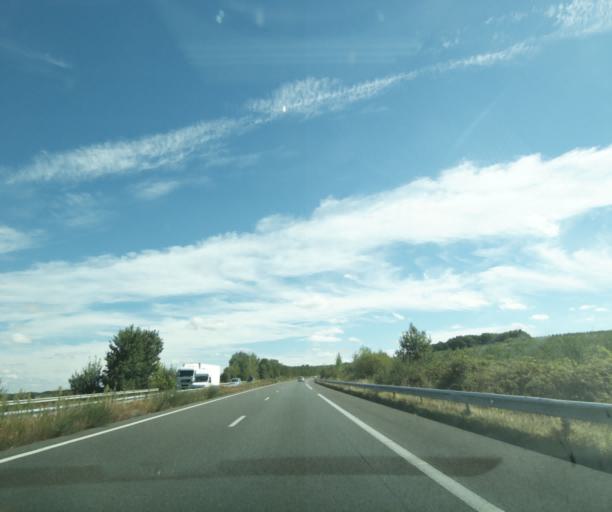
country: FR
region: Midi-Pyrenees
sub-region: Departement du Tarn-et-Garonne
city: Lamagistere
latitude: 44.0928
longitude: 0.7871
